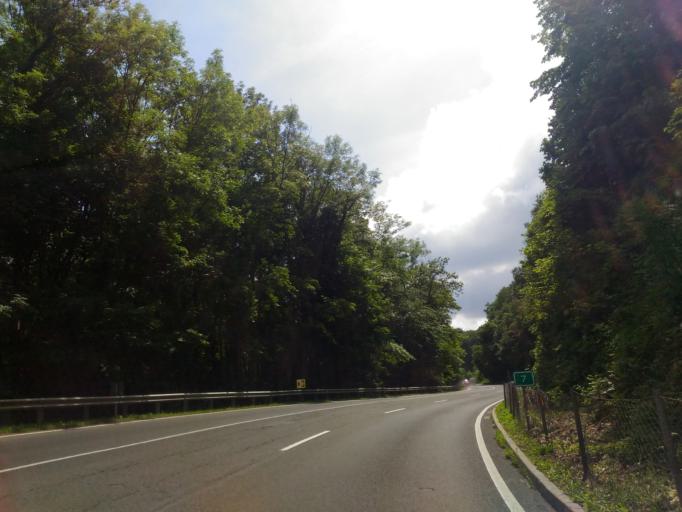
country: HU
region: Baranya
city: Komlo
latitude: 46.1454
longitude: 18.2499
